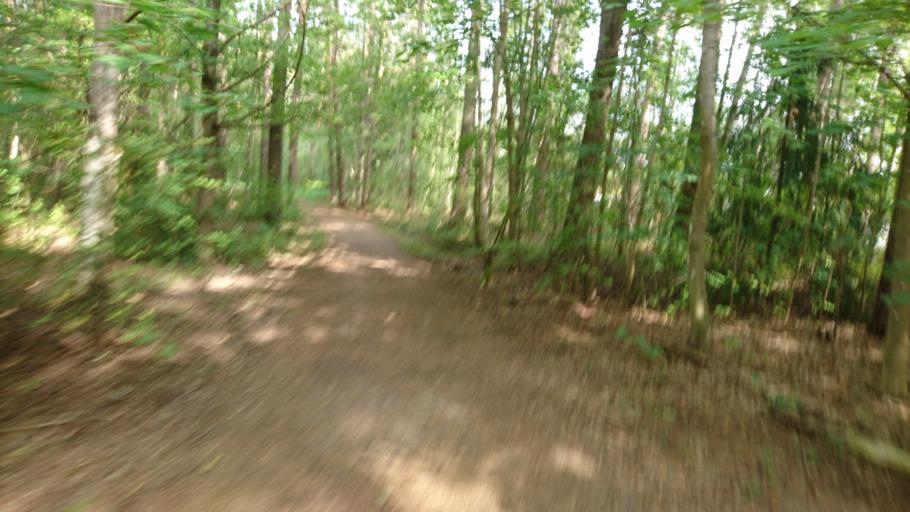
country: SE
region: Uppsala
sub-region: Uppsala Kommun
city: Uppsala
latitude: 59.8447
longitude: 17.6209
